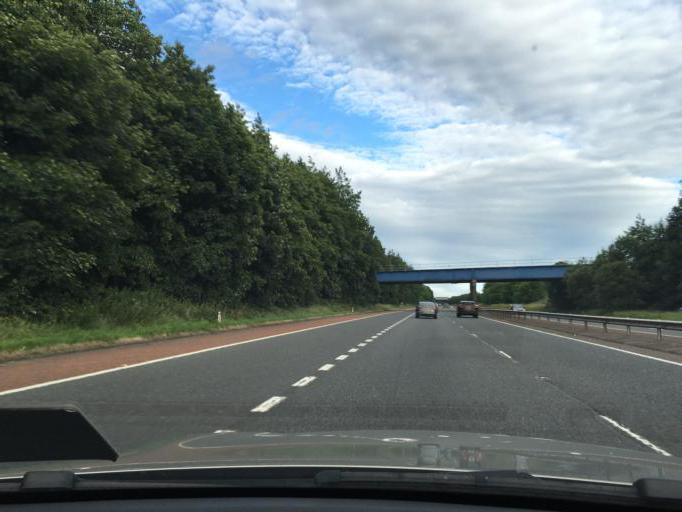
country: GB
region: Northern Ireland
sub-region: Antrim Borough
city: Templepatrick
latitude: 54.7096
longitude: -6.0678
